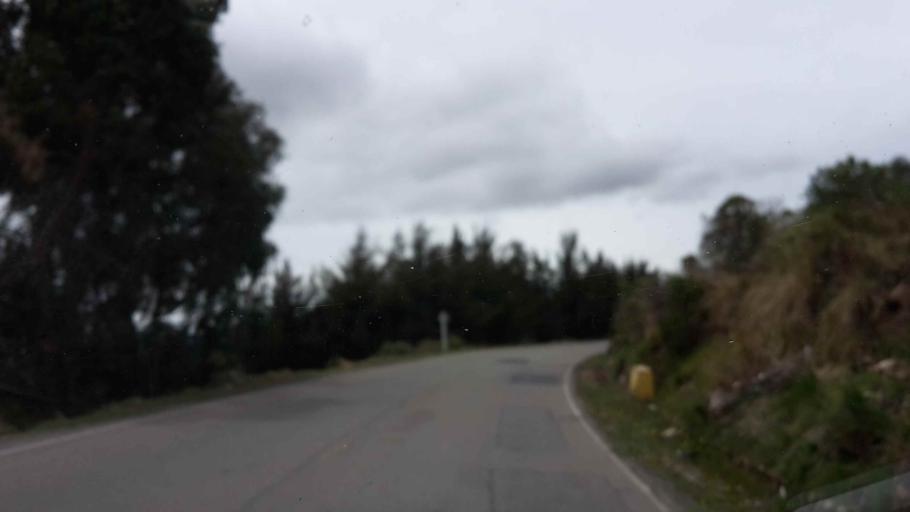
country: BO
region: Cochabamba
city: Arani
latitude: -17.4732
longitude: -65.6490
